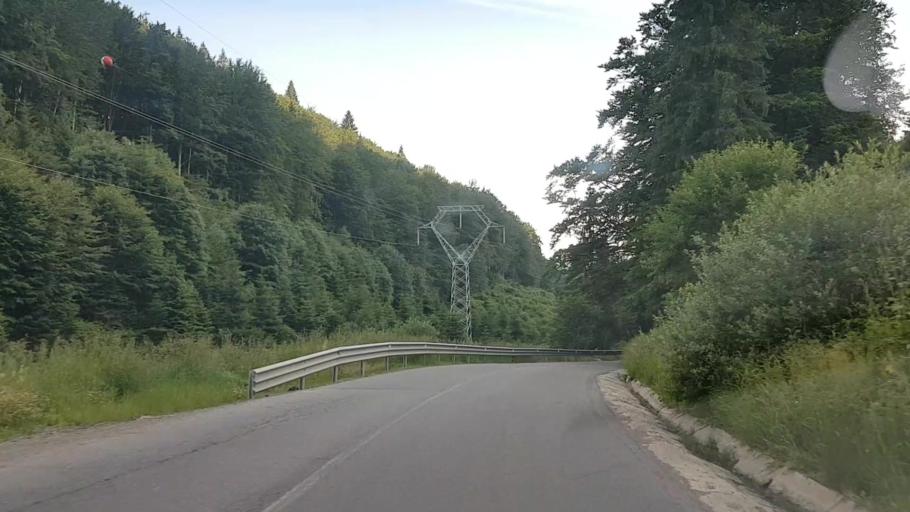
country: RO
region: Harghita
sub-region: Comuna Praid
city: Ocna de Sus
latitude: 46.6197
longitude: 25.2505
